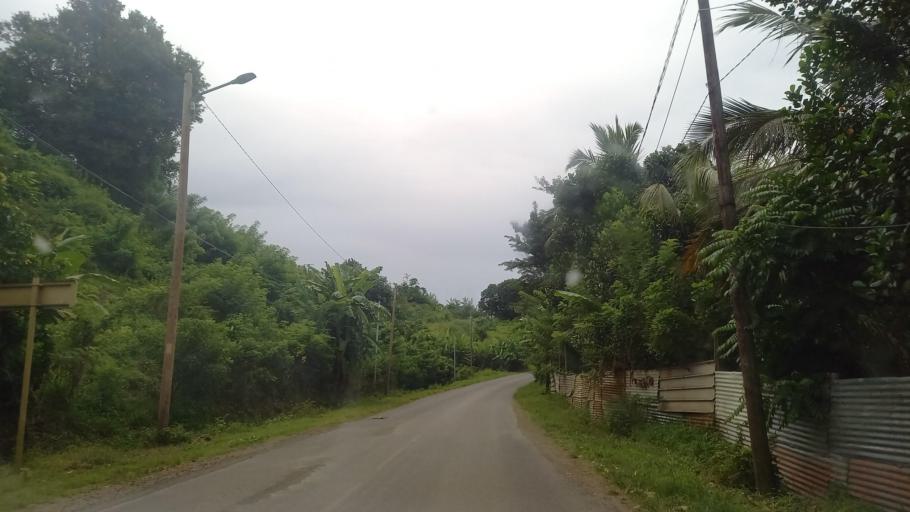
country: YT
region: Kani-Keli
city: Kani Keli
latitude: -12.9245
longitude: 45.1056
